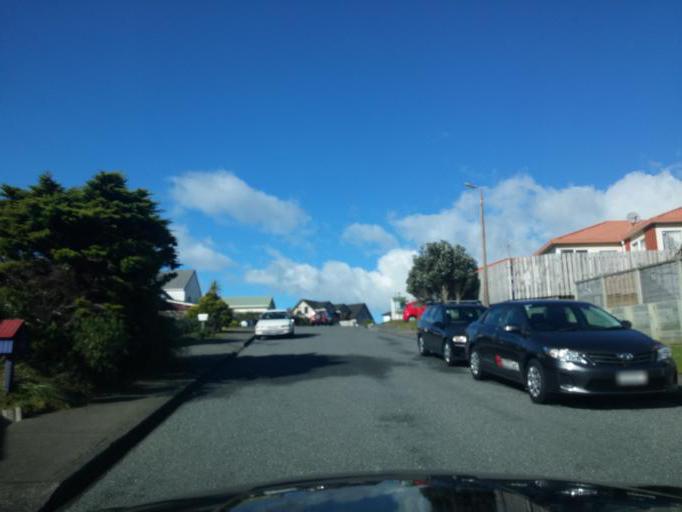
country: NZ
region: Wellington
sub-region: Wellington City
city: Wellington
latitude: -41.2351
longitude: 174.7926
